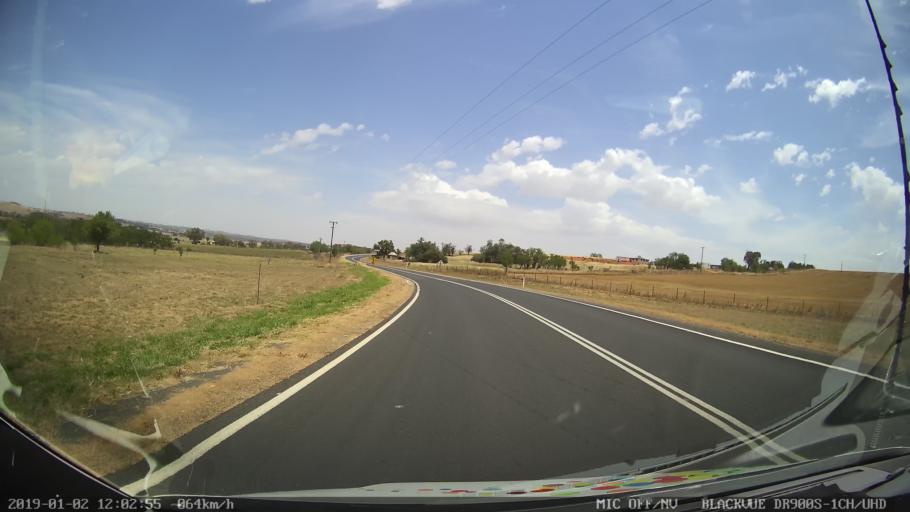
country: AU
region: New South Wales
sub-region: Young
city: Young
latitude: -34.5350
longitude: 148.3264
